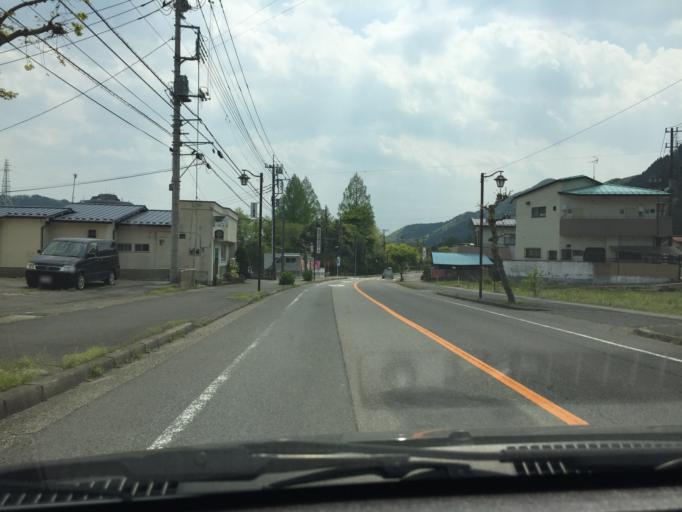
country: JP
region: Tochigi
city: Imaichi
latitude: 36.8300
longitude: 139.7155
